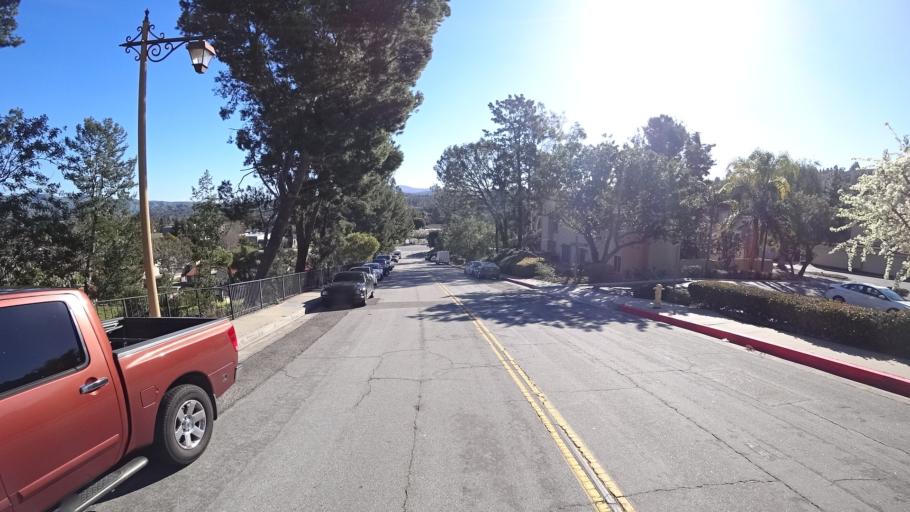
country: US
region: California
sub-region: Orange County
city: Villa Park
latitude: 33.8464
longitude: -117.7921
